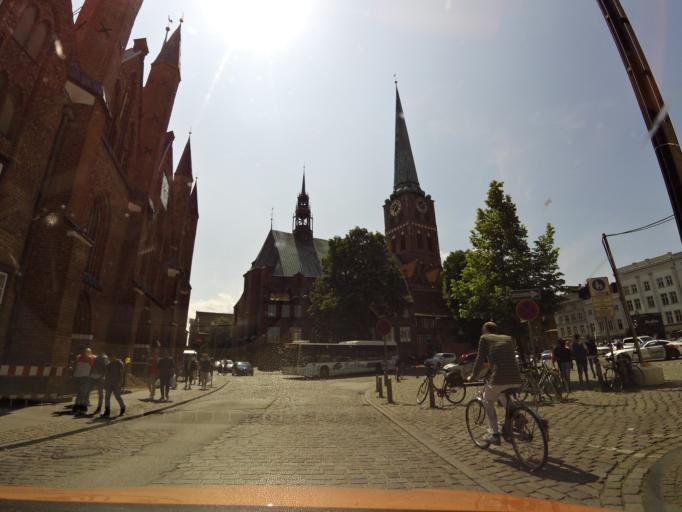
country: DE
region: Schleswig-Holstein
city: Luebeck
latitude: 53.8715
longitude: 10.6899
